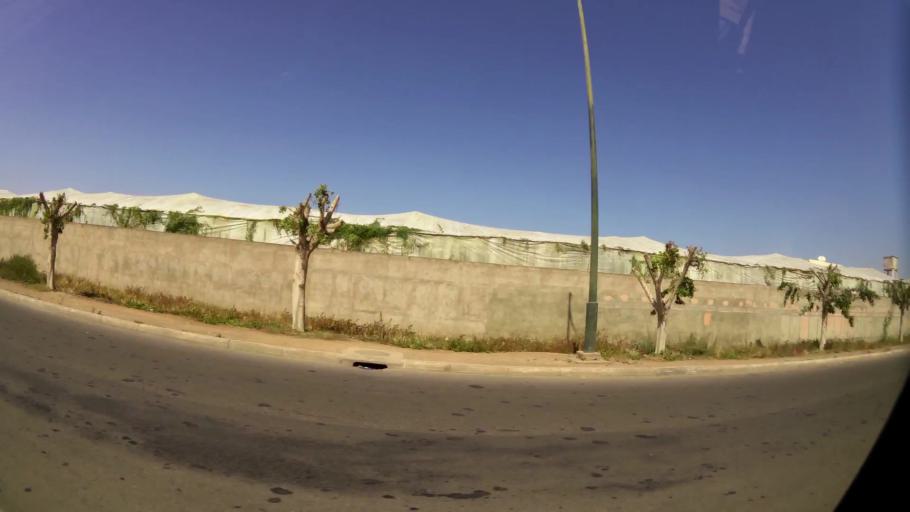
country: MA
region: Souss-Massa-Draa
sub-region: Inezgane-Ait Mellou
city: Inezgane
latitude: 30.3420
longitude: -9.5081
